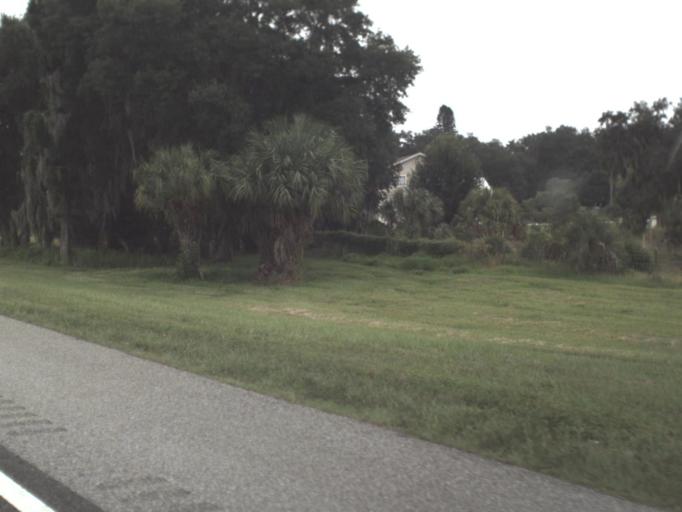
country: US
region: Florida
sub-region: Manatee County
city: Memphis
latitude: 27.5835
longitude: -82.5594
